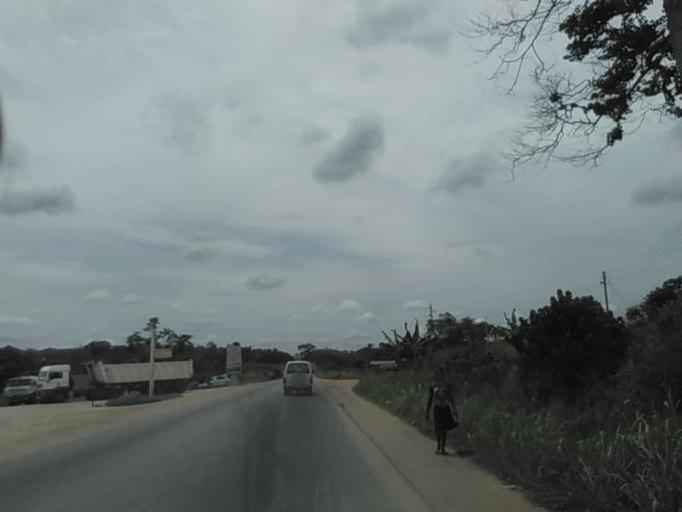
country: GH
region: Ashanti
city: Mamponteng
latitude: 6.8431
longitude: -1.5151
